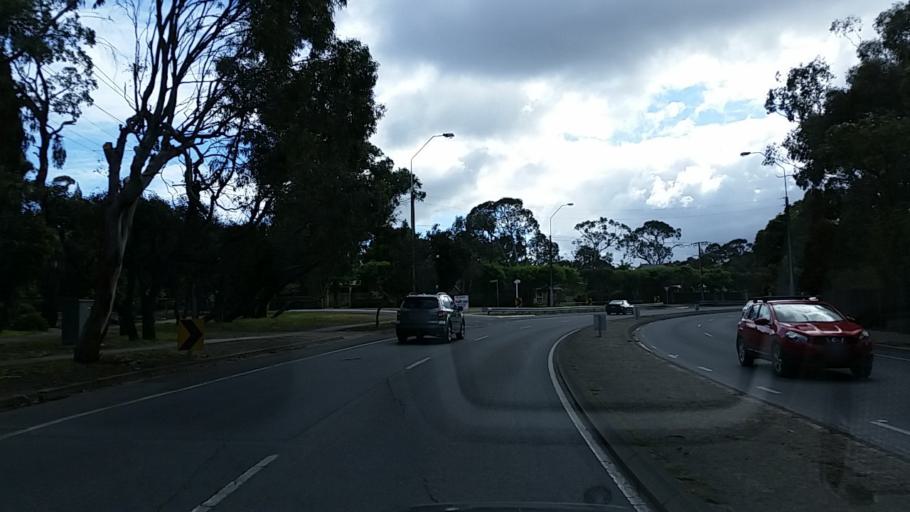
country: AU
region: South Australia
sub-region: Mitcham
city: Blackwood
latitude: -35.0217
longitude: 138.6086
